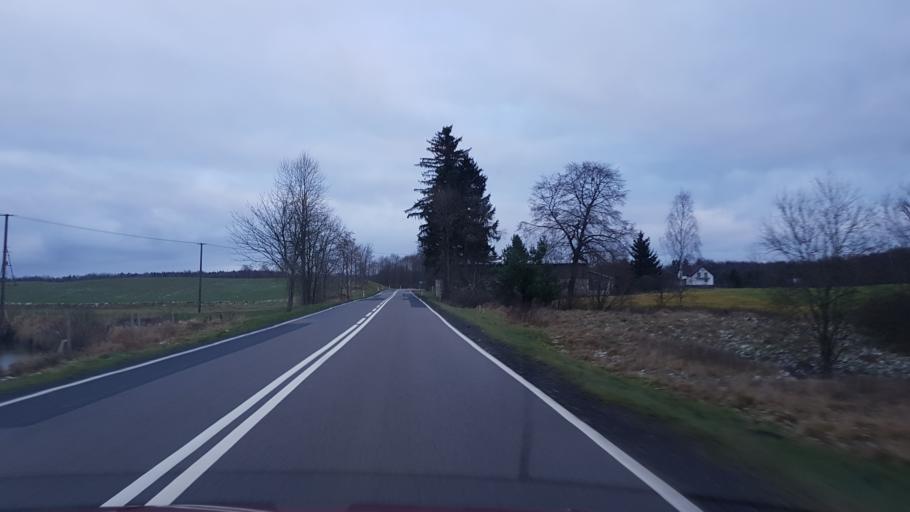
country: PL
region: Pomeranian Voivodeship
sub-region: Powiat bytowski
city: Tuchomie
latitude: 54.0634
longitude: 17.2502
